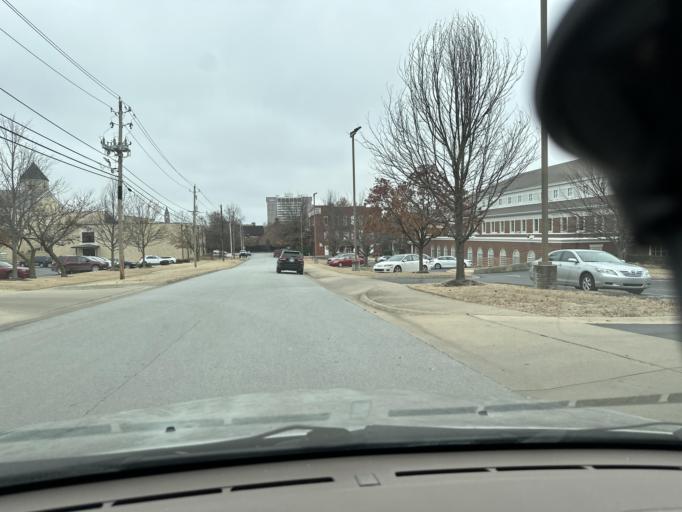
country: US
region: Arkansas
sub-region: Washington County
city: Fayetteville
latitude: 36.0680
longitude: -94.1590
